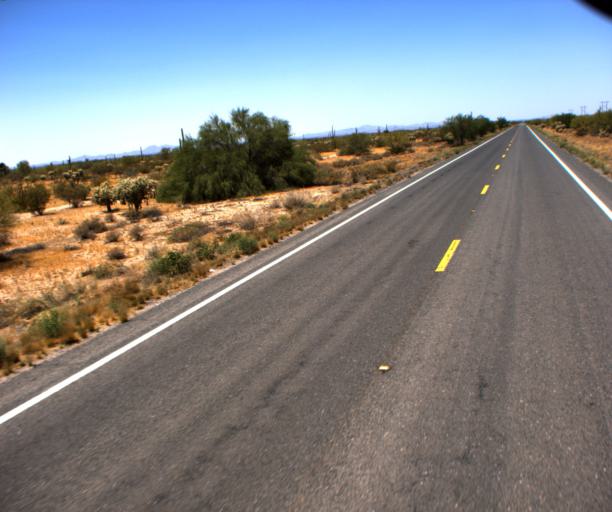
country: US
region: Arizona
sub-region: Pinal County
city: Florence
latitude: 32.8954
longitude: -111.2735
